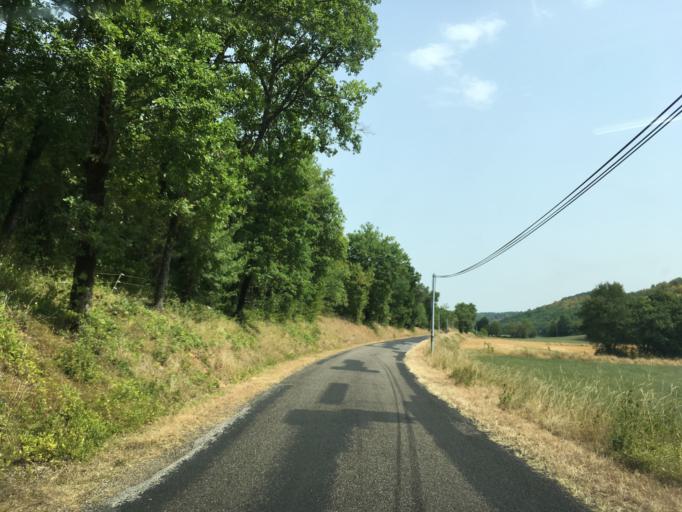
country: FR
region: Midi-Pyrenees
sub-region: Departement du Lot
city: Le Vigan
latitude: 44.7450
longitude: 1.5227
